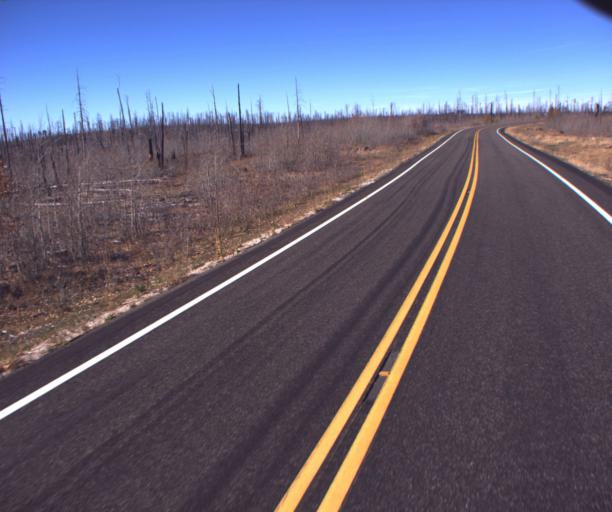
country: US
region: Arizona
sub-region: Coconino County
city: Fredonia
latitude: 36.5705
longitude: -112.1739
